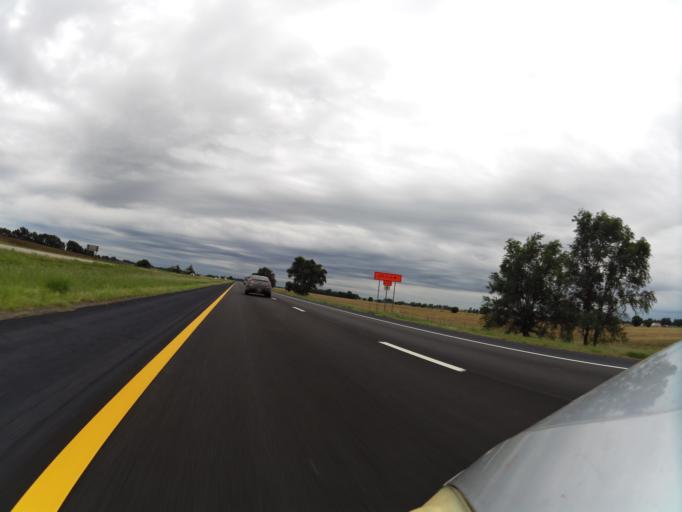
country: US
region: Kansas
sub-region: Sedgwick County
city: Colwich
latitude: 37.8678
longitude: -97.6231
